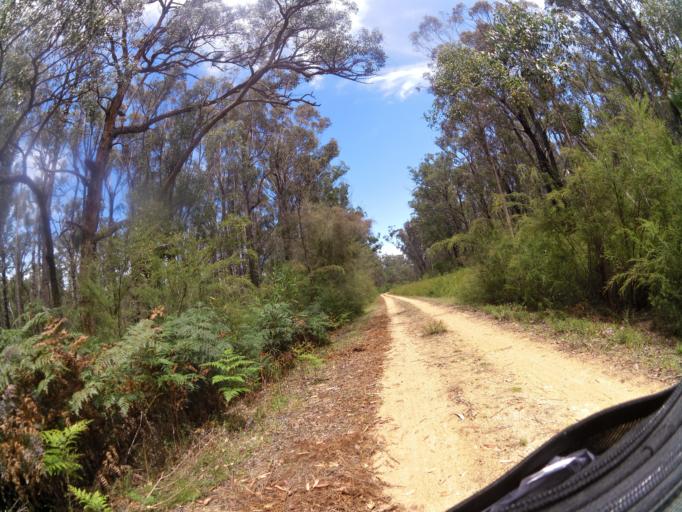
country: AU
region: Victoria
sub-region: East Gippsland
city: Lakes Entrance
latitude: -37.7447
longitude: 147.9986
